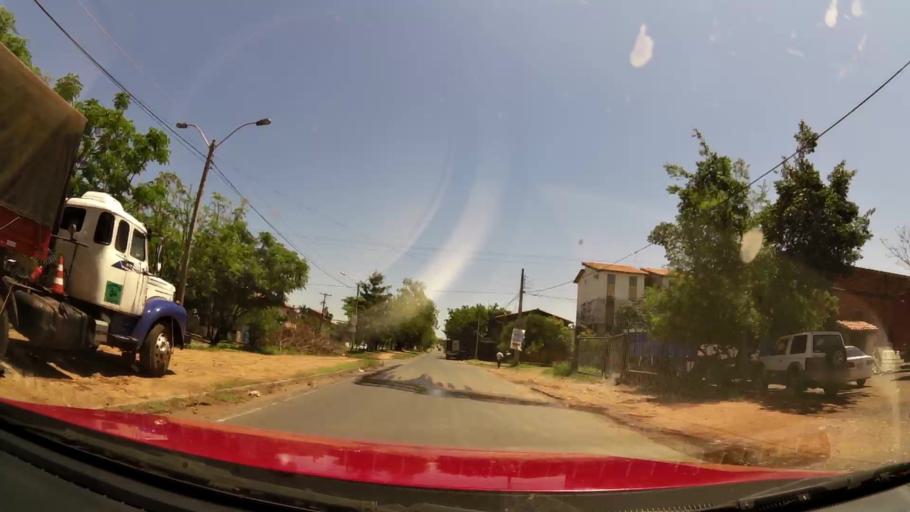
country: PY
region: Central
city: Colonia Mariano Roque Alonso
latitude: -25.2350
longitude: -57.5432
